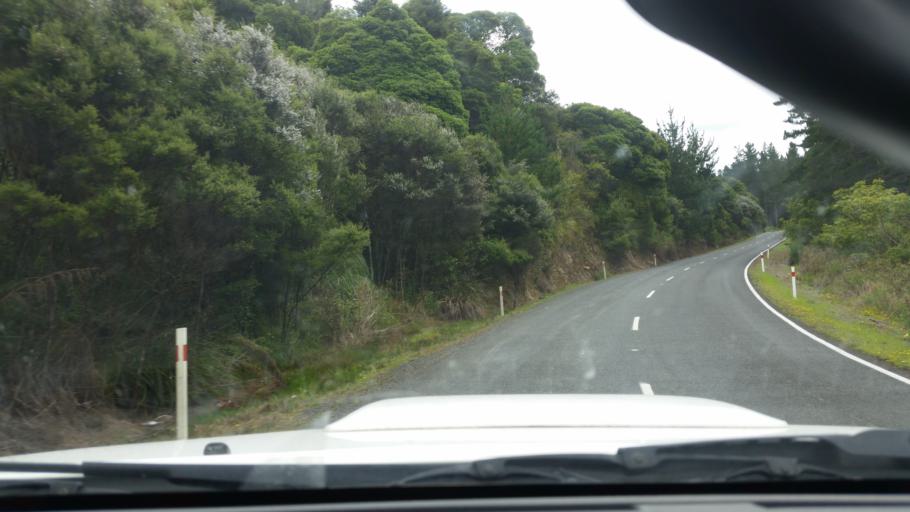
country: NZ
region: Northland
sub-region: Kaipara District
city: Dargaville
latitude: -35.7364
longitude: 173.8650
